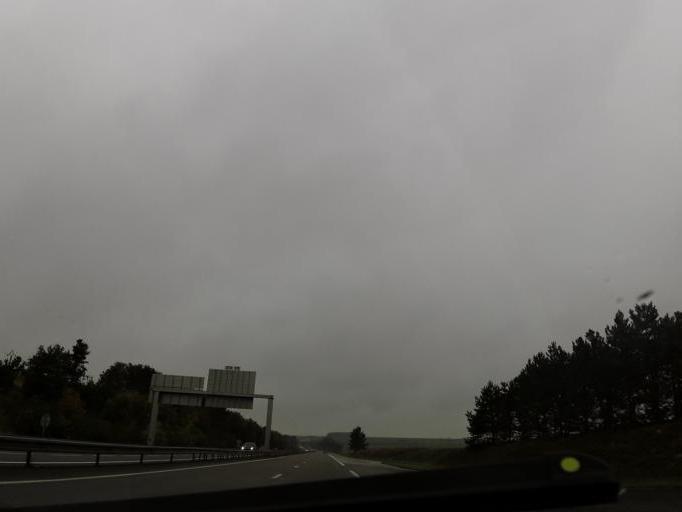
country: FR
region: Champagne-Ardenne
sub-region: Departement de la Marne
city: Fagnieres
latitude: 49.0440
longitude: 4.3187
